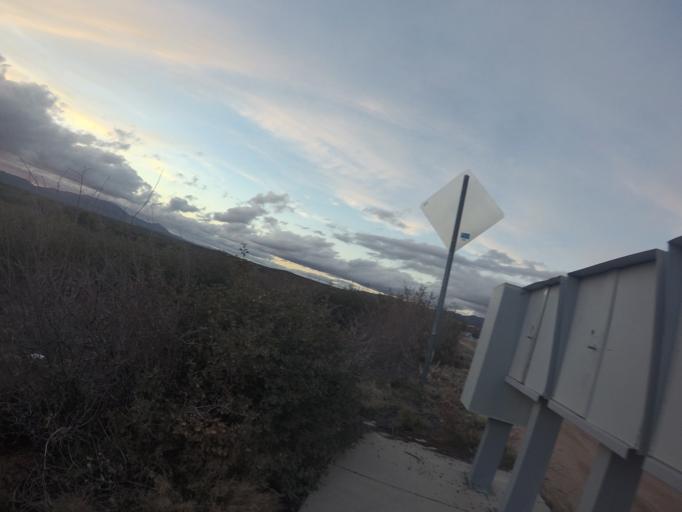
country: US
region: Arizona
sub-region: Yavapai County
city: Prescott
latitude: 34.4121
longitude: -112.6105
